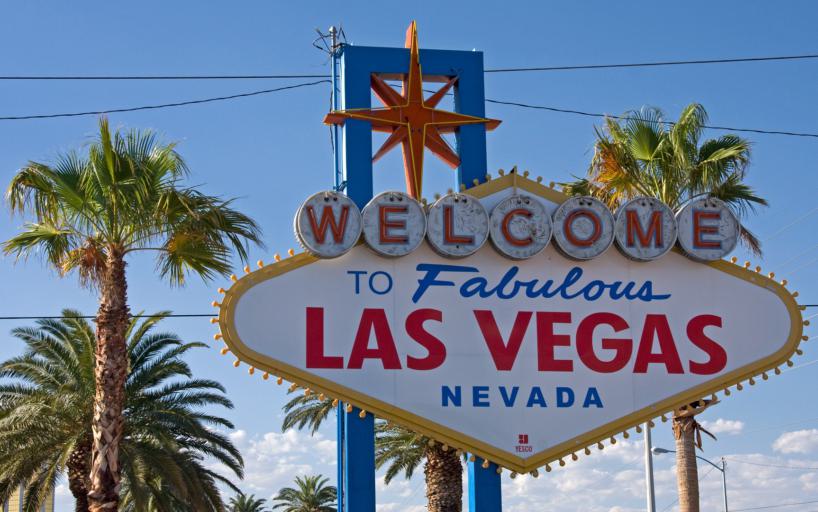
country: US
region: Nevada
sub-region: Clark County
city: Paradise
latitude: 36.0820
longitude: -115.1728
